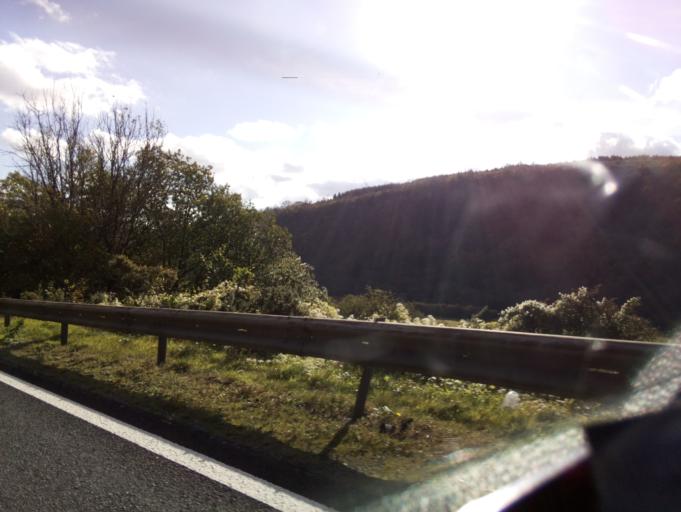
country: GB
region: Wales
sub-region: Merthyr Tydfil County Borough
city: Merthyr Tydfil
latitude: 51.7822
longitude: -3.4237
